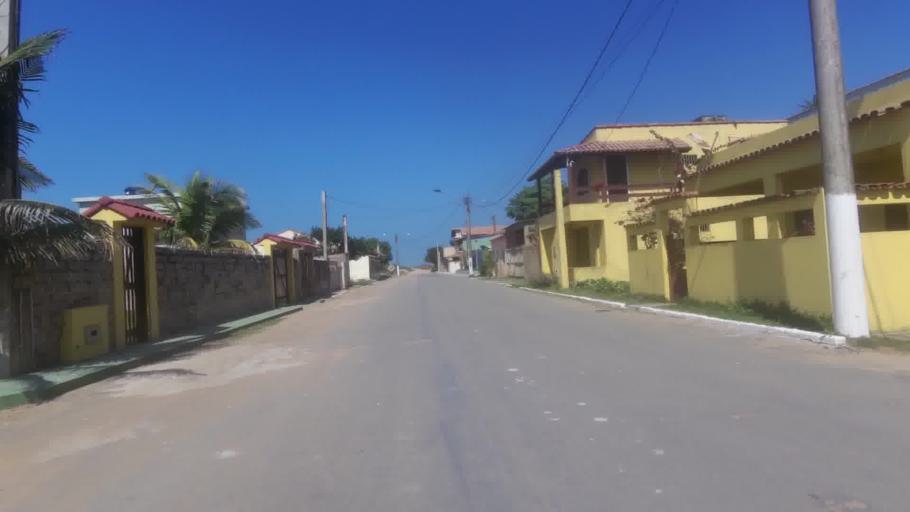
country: BR
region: Espirito Santo
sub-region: Marataizes
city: Marataizes
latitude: -21.0926
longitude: -40.8452
